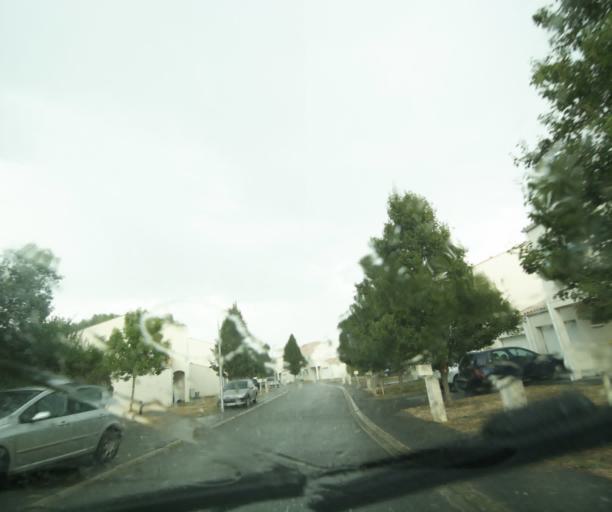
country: FR
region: Poitou-Charentes
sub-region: Departement de la Charente-Maritime
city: Tonnay-Charente
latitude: 45.9501
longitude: -0.8748
